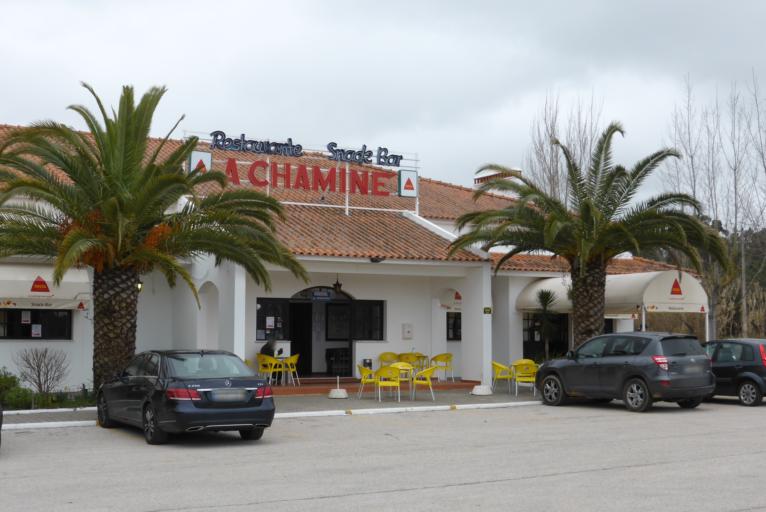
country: PT
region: Setubal
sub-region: Grandola
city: Grandola
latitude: 38.2161
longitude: -8.5580
